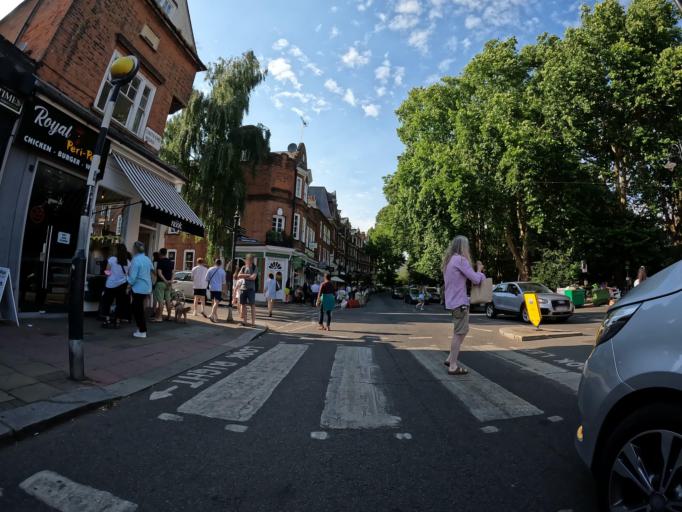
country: GB
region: England
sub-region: Greater London
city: Barnet
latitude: 51.6350
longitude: -0.2044
